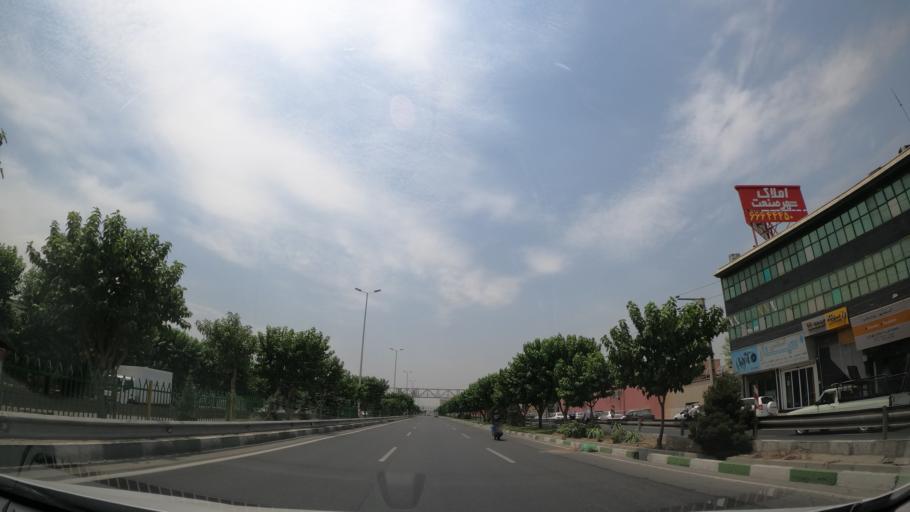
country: IR
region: Tehran
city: Tehran
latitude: 35.6752
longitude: 51.3182
